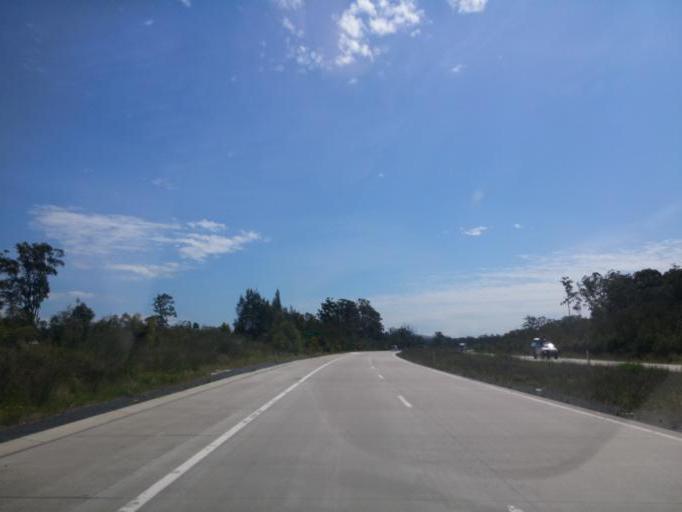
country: AU
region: New South Wales
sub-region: Great Lakes
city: Bulahdelah
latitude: -32.4380
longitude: 152.1923
